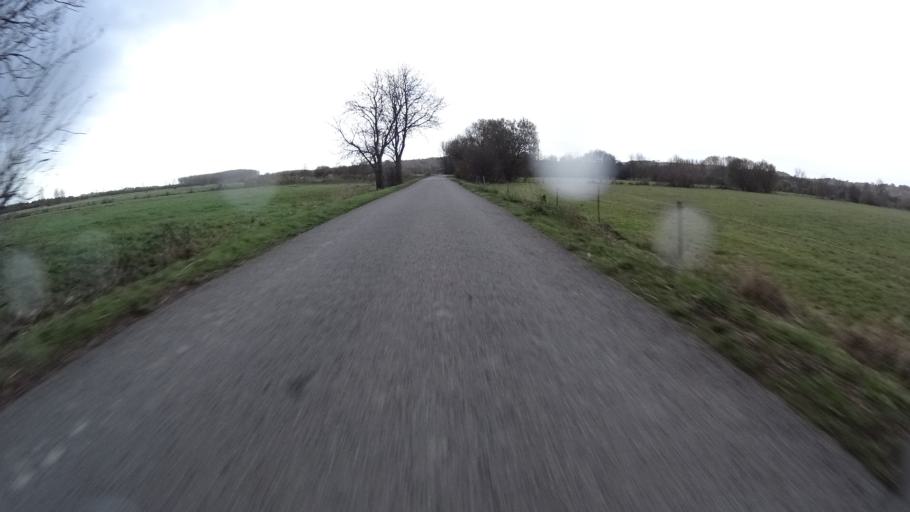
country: FR
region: Brittany
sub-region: Departement d'Ille-et-Vilaine
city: Sainte-Marie
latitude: 47.6697
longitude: -2.0313
